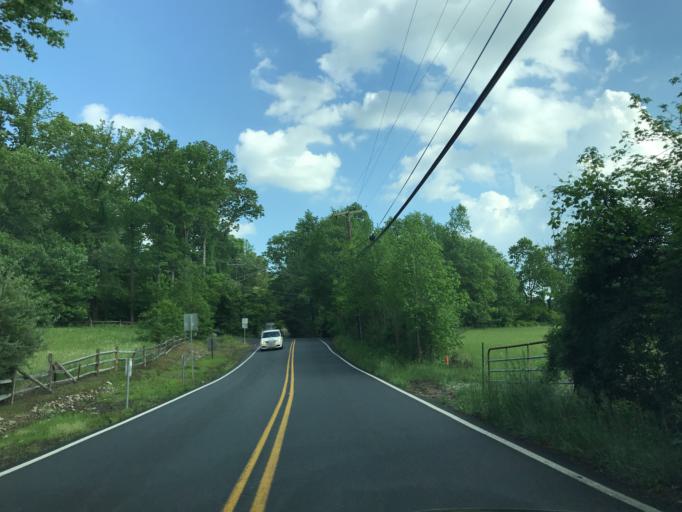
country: US
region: Maryland
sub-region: Harford County
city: Bel Air North
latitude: 39.5388
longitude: -76.3930
